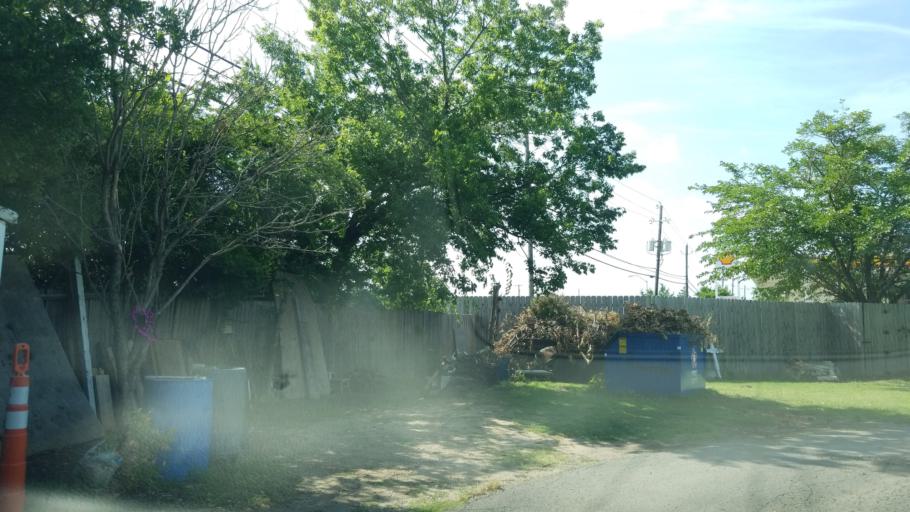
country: US
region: Texas
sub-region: Dallas County
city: Farmers Branch
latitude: 32.8793
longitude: -96.8855
